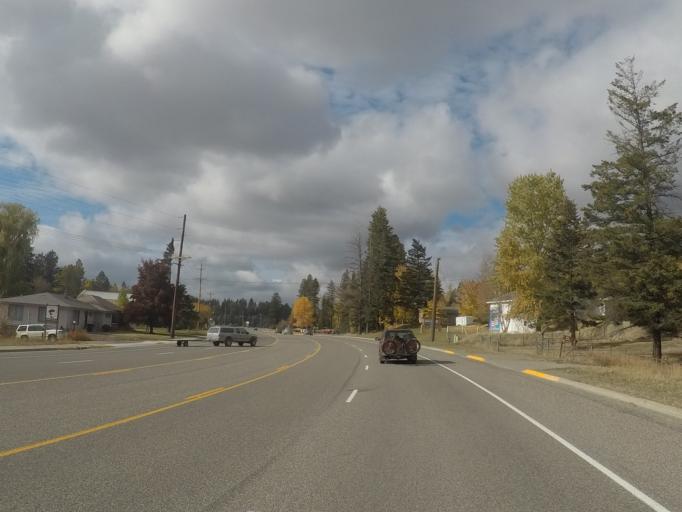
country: US
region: Montana
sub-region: Flathead County
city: Columbia Falls
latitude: 48.3660
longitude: -114.1690
